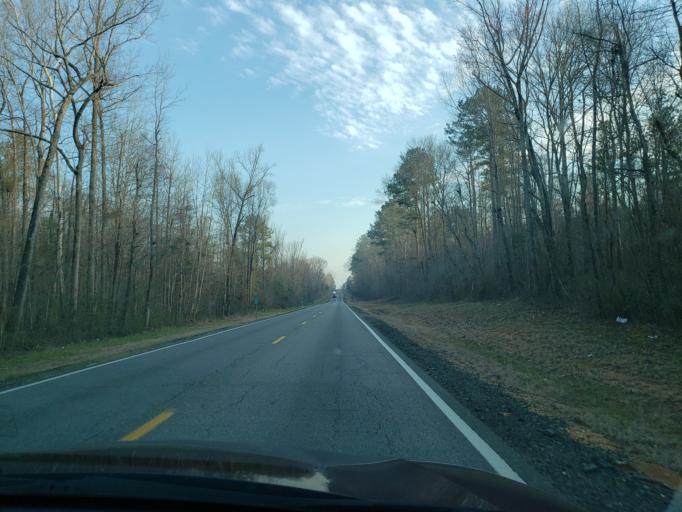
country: US
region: Alabama
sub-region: Hale County
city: Greensboro
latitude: 32.7984
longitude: -87.5922
